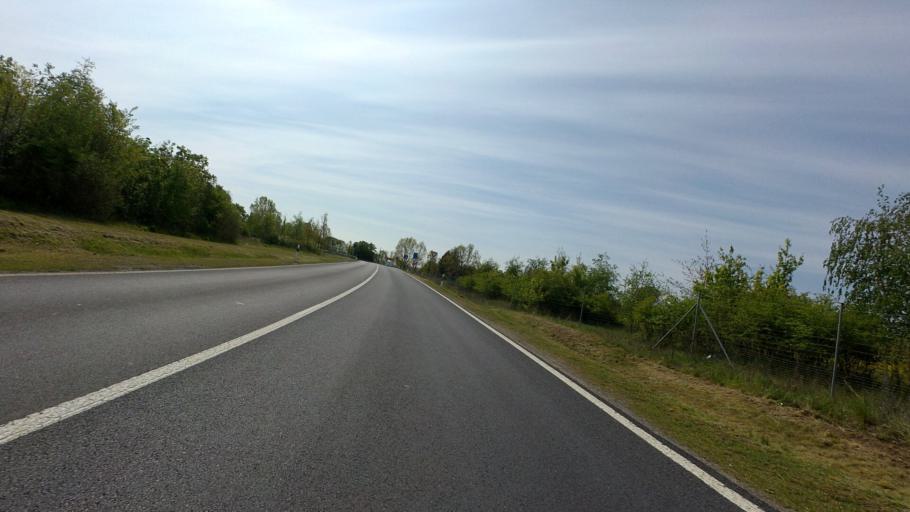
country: DE
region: Brandenburg
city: Mittenwalde
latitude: 52.2925
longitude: 13.5575
